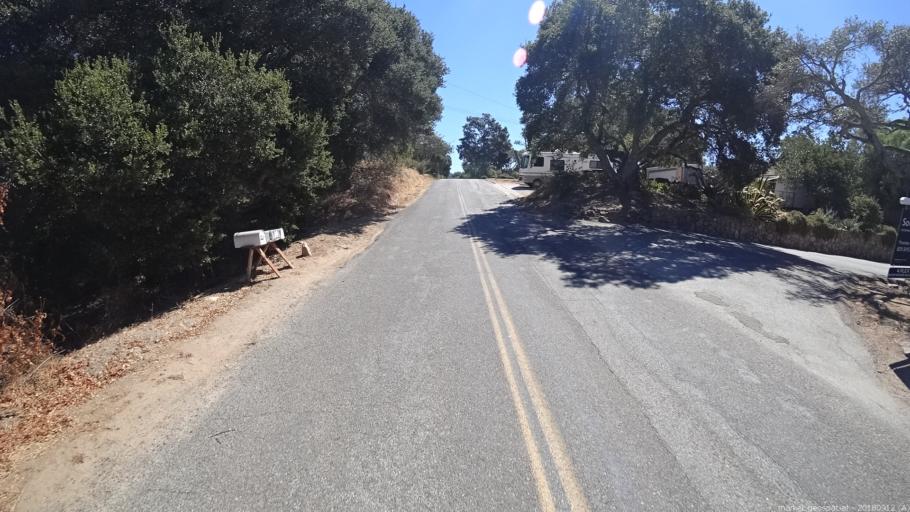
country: US
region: California
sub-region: Monterey County
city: Carmel Valley Village
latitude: 36.4807
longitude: -121.7253
